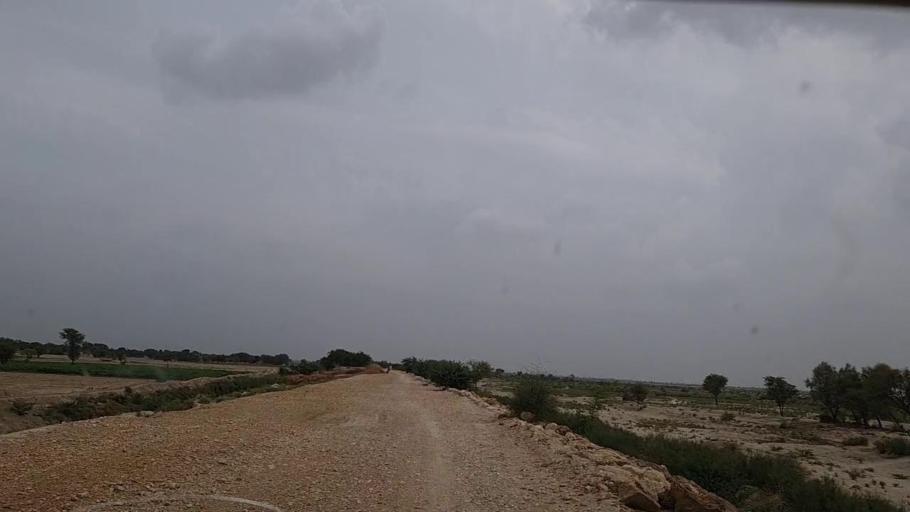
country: PK
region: Sindh
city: Johi
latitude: 26.7210
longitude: 67.5791
